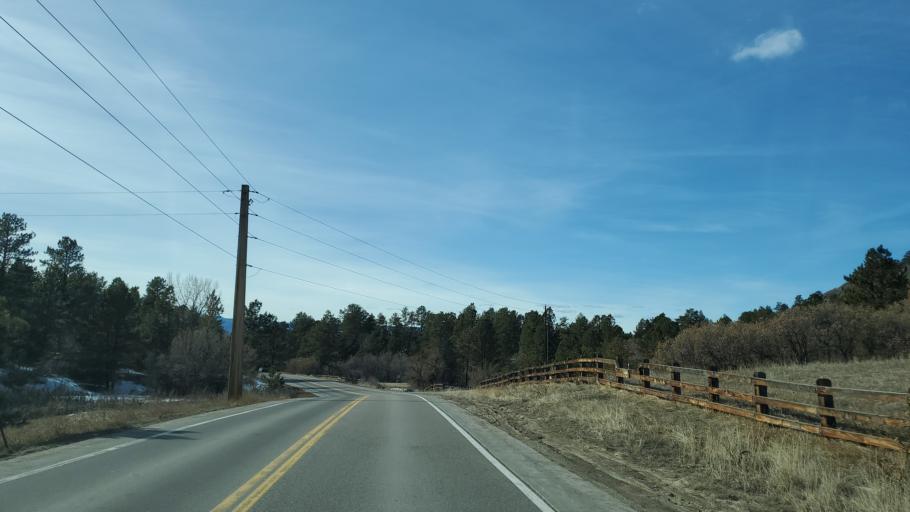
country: US
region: Colorado
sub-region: Douglas County
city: Castle Pines
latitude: 39.4446
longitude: -104.8815
